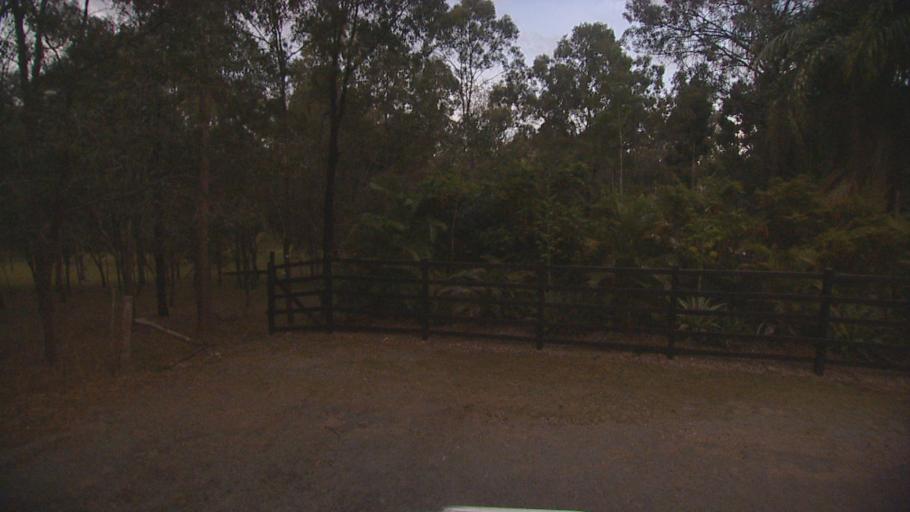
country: AU
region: Queensland
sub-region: Logan
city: Chambers Flat
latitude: -27.8181
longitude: 153.0918
